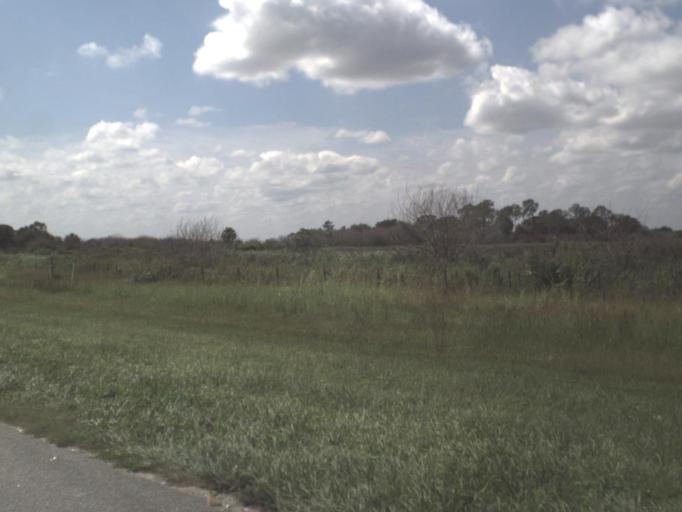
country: US
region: Florida
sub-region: Hendry County
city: Port LaBelle
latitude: 26.6442
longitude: -81.4363
